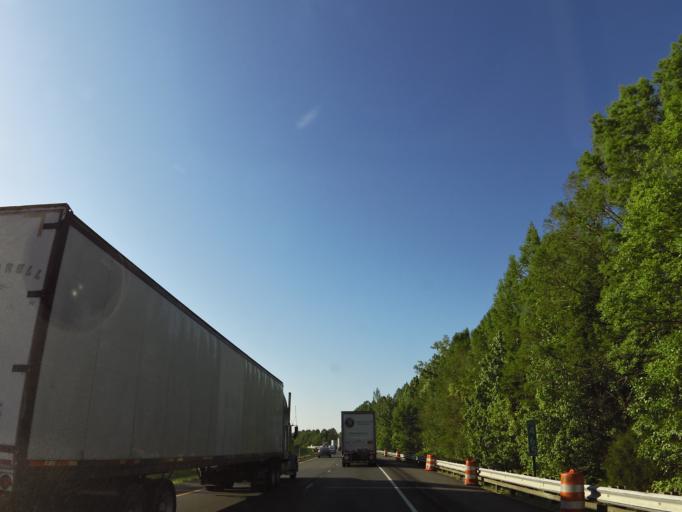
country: US
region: Indiana
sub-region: Jackson County
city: Seymour
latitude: 38.9163
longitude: -85.8346
